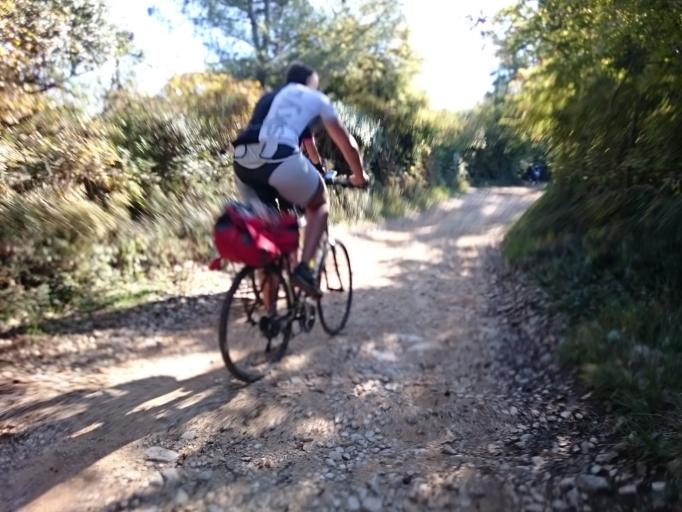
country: HR
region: Istarska
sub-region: Grad Porec
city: Porec
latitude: 45.2565
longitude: 13.5898
